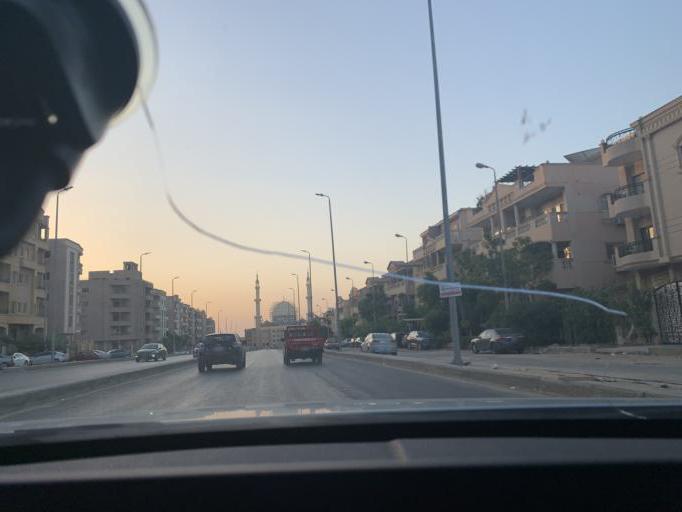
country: EG
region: Muhafazat al Qahirah
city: Cairo
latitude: 30.0027
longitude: 31.4600
